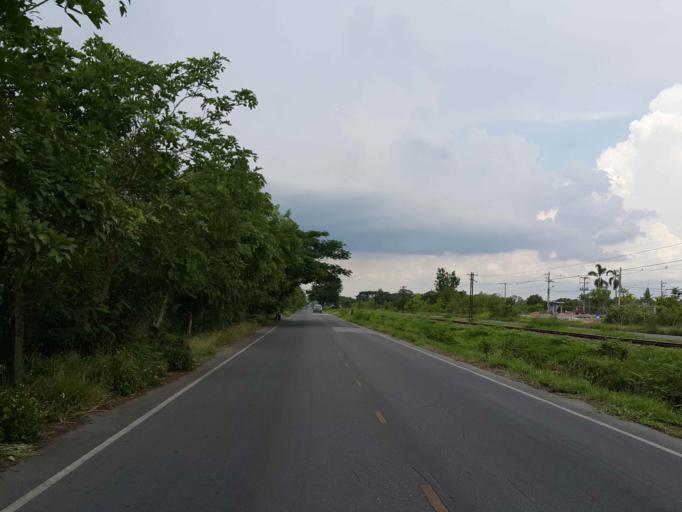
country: TH
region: Chiang Mai
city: Saraphi
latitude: 18.7446
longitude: 99.0271
